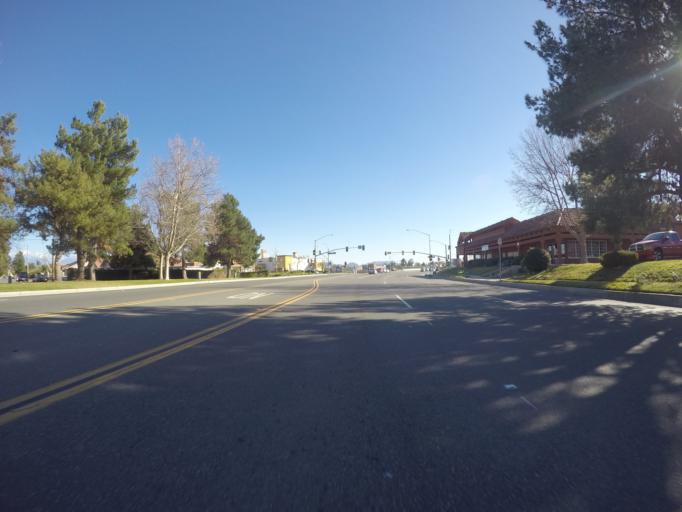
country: US
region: California
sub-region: San Bernardino County
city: Muscoy
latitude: 34.1384
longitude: -117.3712
